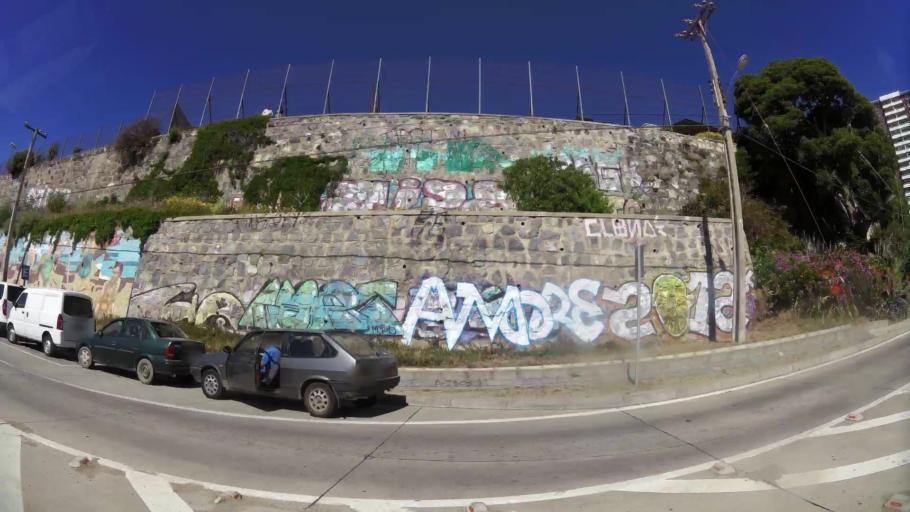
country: CL
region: Valparaiso
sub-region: Provincia de Valparaiso
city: Valparaiso
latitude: -33.0222
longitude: -71.6437
